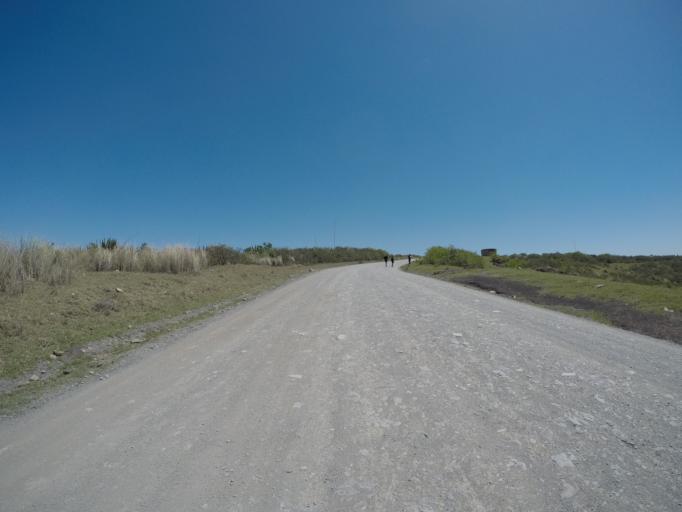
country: ZA
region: Eastern Cape
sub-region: OR Tambo District Municipality
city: Libode
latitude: -31.9760
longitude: 29.0349
